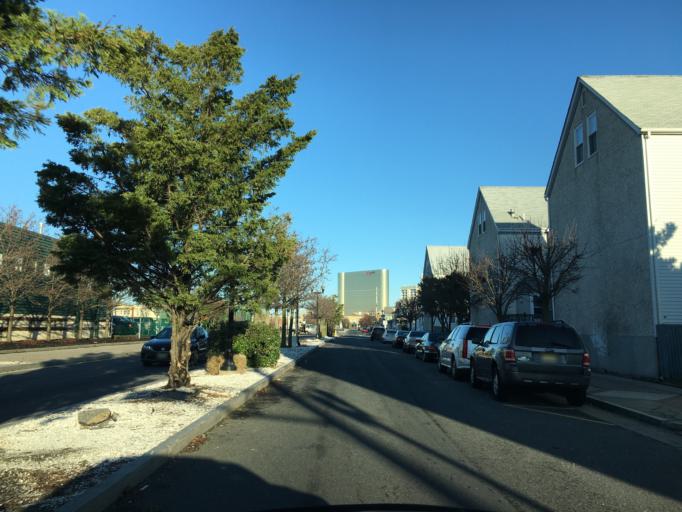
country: US
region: New Jersey
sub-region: Atlantic County
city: Atlantic City
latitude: 39.3662
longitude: -74.4276
